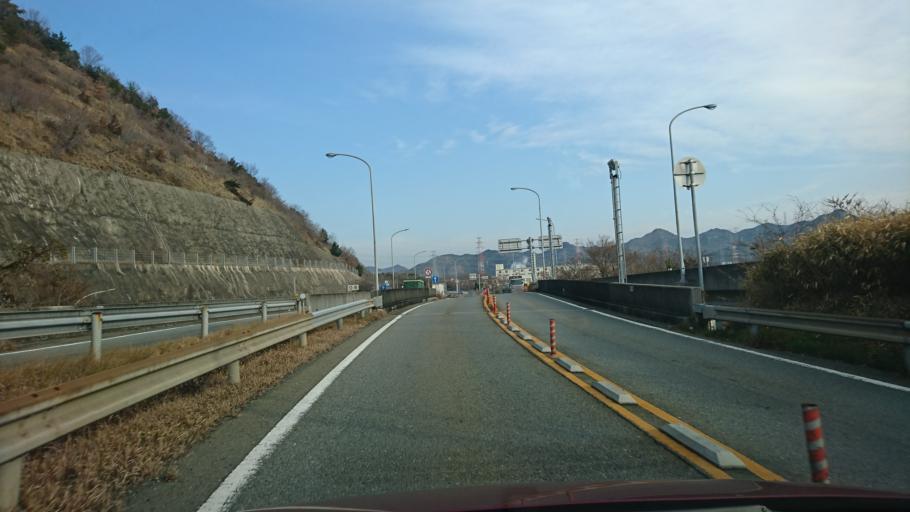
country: JP
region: Hyogo
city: Shirahamacho-usazakiminami
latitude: 34.8012
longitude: 134.7431
